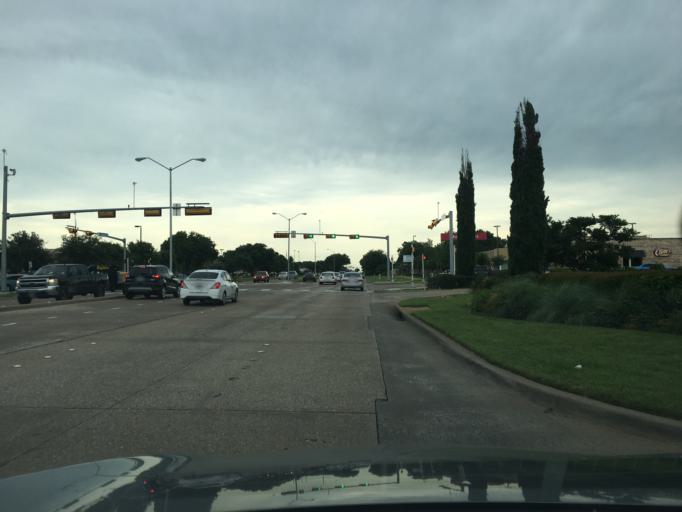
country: US
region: Texas
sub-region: Dallas County
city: Richardson
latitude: 32.9438
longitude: -96.7000
